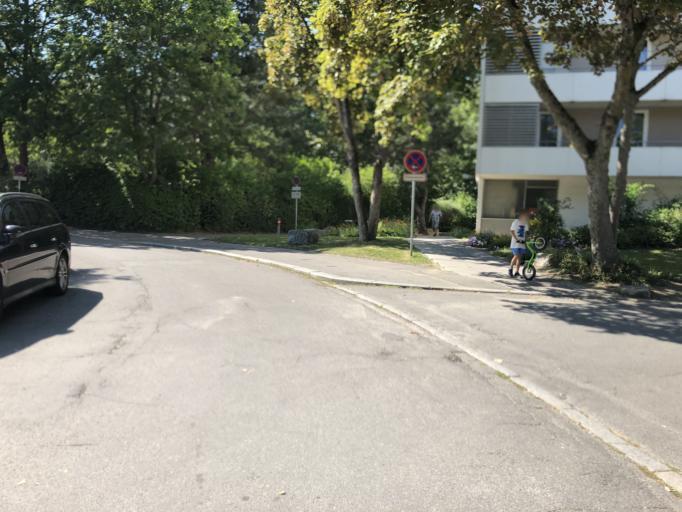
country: DE
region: Baden-Wuerttemberg
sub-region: Regierungsbezirk Stuttgart
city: Magstadt
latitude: 48.7314
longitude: 8.9994
